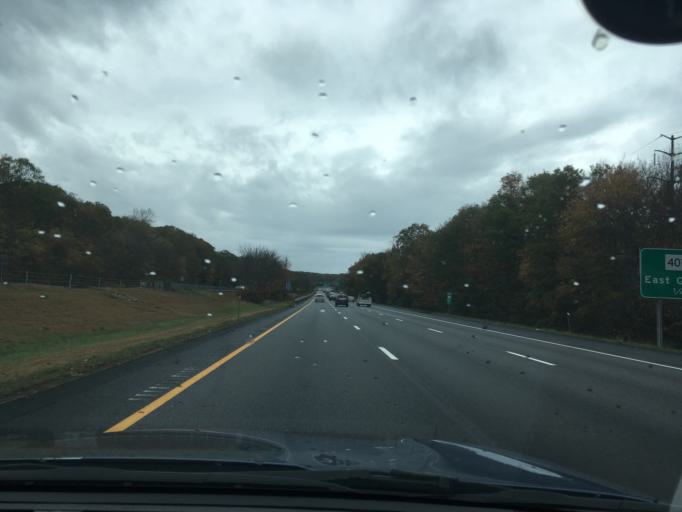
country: US
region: Rhode Island
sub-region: Kent County
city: East Greenwich
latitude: 41.6565
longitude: -71.4892
